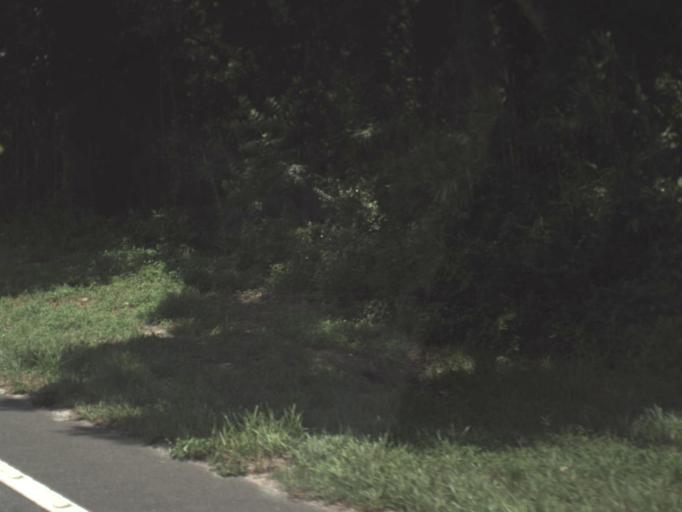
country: US
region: Florida
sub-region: Alachua County
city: Archer
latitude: 29.5181
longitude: -82.4064
